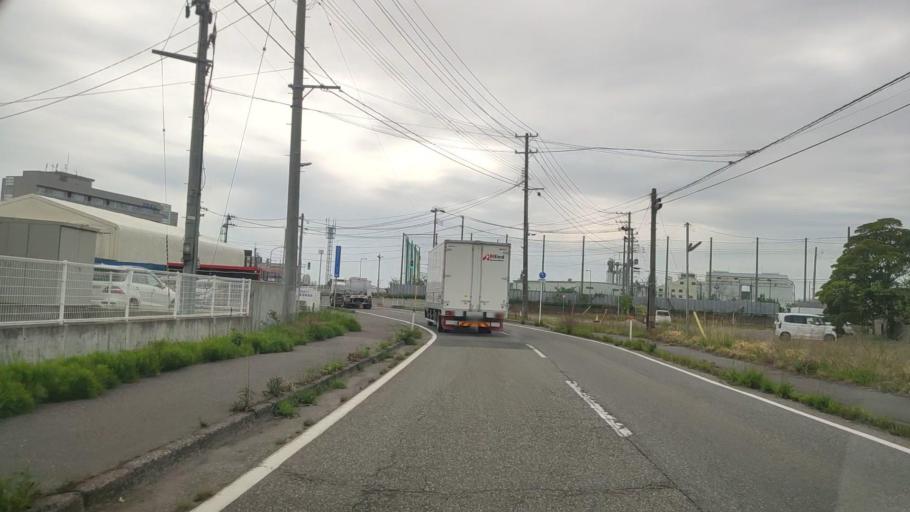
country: JP
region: Niigata
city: Niigata-shi
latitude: 37.9476
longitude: 139.0779
